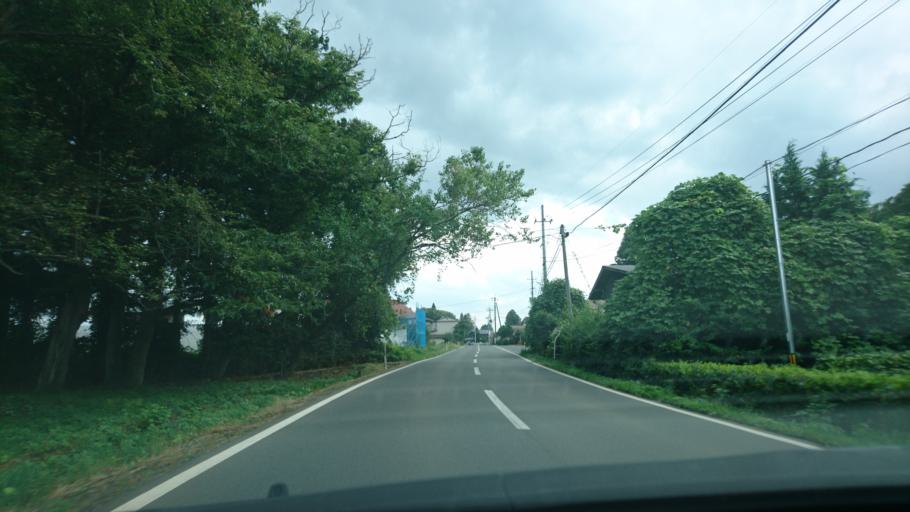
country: JP
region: Iwate
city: Hanamaki
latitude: 39.3718
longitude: 141.1454
